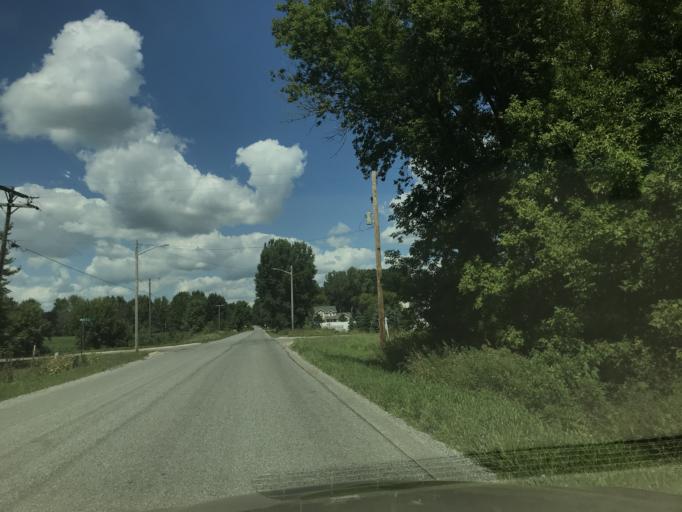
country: US
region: Michigan
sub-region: Ingham County
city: Holt
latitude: 42.6252
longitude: -84.5627
